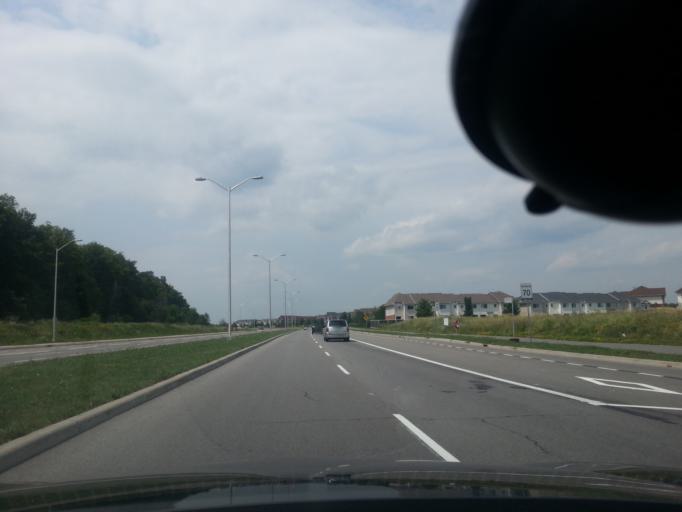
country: CA
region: Ontario
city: Bells Corners
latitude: 45.2728
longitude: -75.7099
